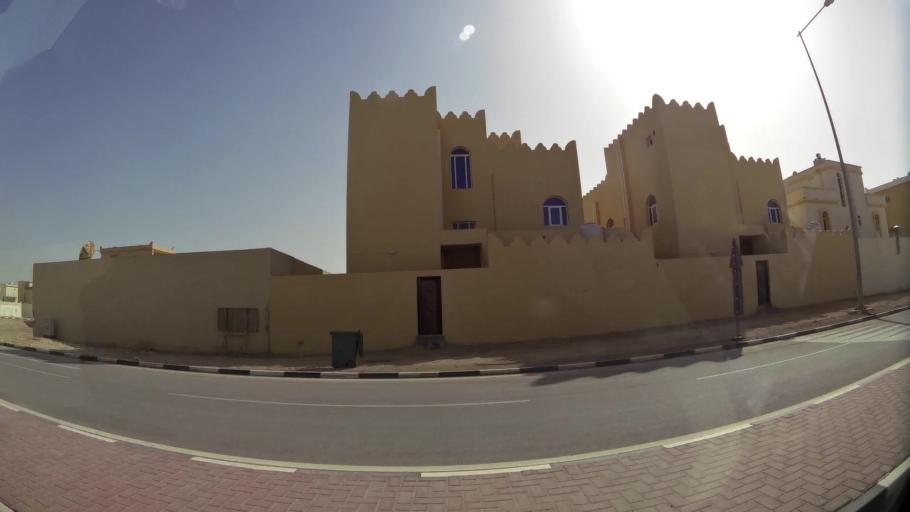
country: QA
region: Baladiyat ar Rayyan
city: Ar Rayyan
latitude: 25.3401
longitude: 51.4242
